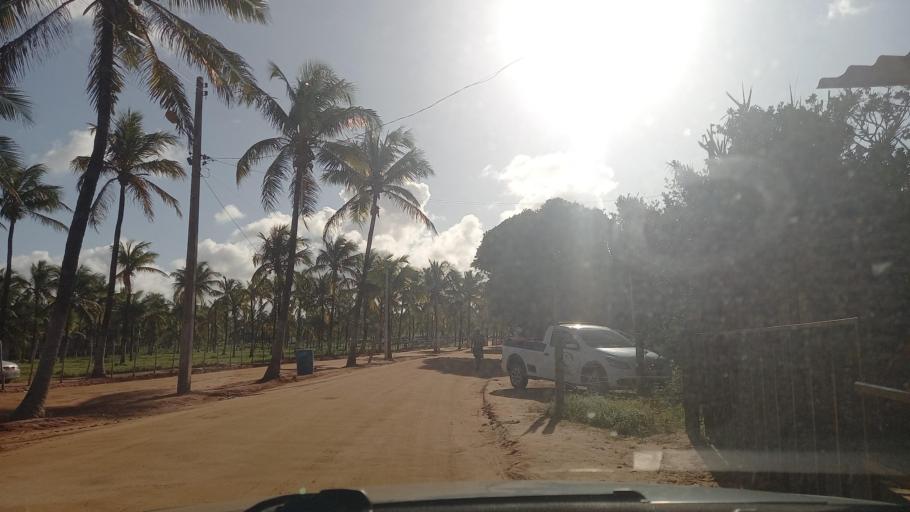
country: BR
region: Alagoas
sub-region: Marechal Deodoro
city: Marechal Deodoro
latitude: -9.8610
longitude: -35.9077
